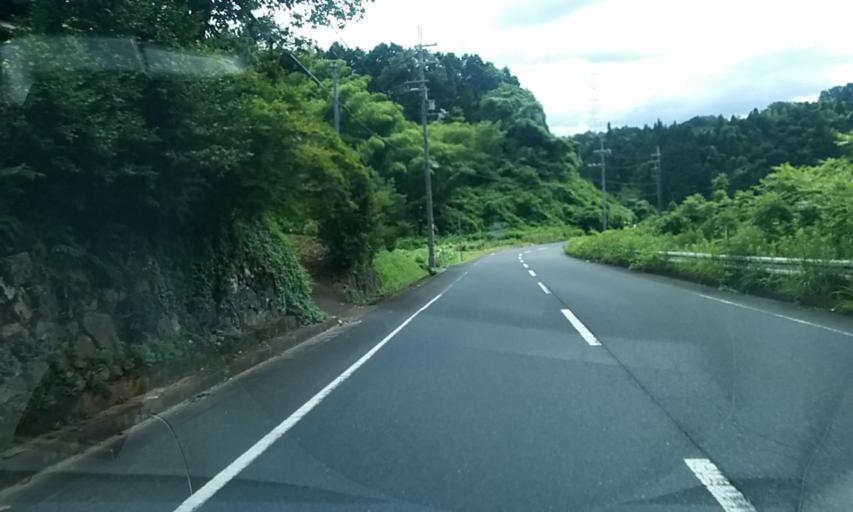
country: JP
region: Kyoto
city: Ayabe
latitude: 35.3467
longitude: 135.2731
